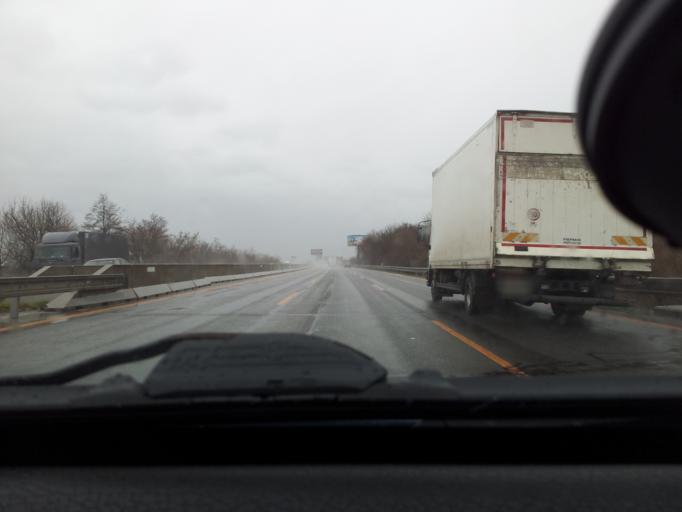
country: SK
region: Bratislavsky
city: Svaty Jur
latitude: 48.2080
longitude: 17.2449
